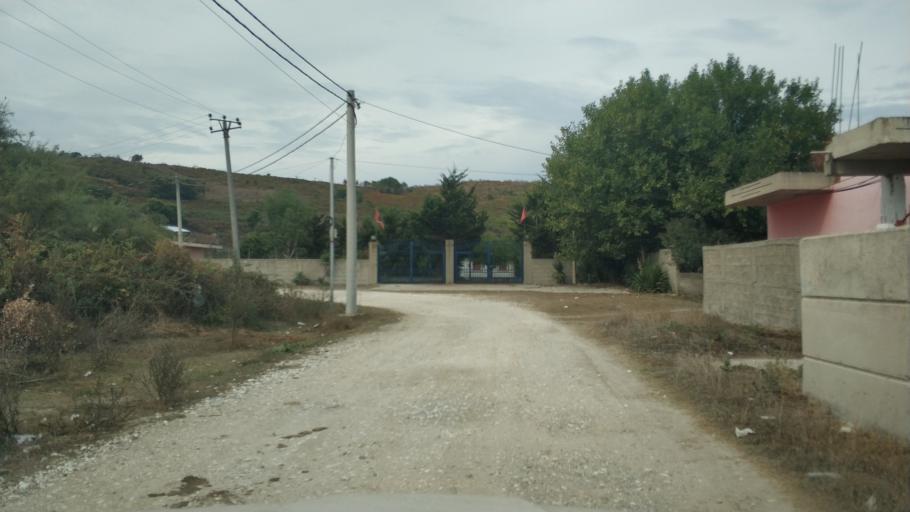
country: AL
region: Vlore
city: Vlore
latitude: 40.5028
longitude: 19.4085
